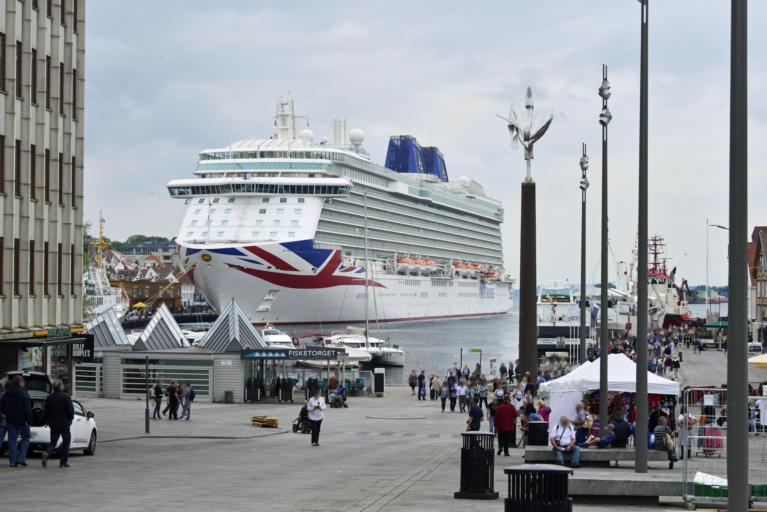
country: NO
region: Rogaland
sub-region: Stavanger
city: Stavanger
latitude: 58.9698
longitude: 5.7316
